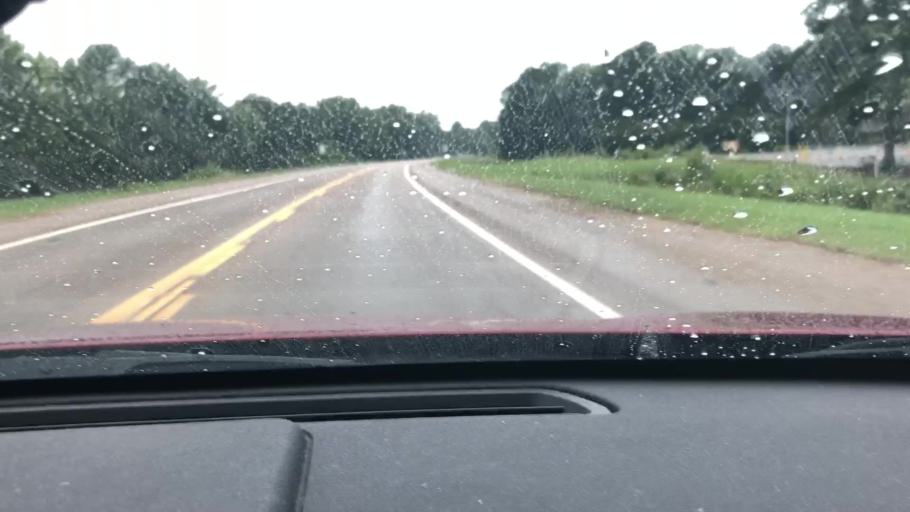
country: US
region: Arkansas
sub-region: Columbia County
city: Magnolia
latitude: 33.2964
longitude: -93.2539
